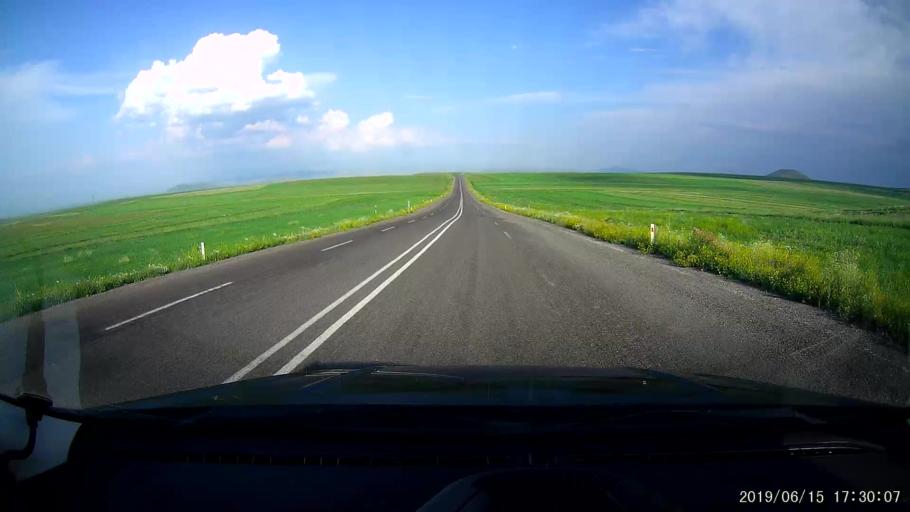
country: TR
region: Kars
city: Basgedikler
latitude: 40.5847
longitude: 43.4632
